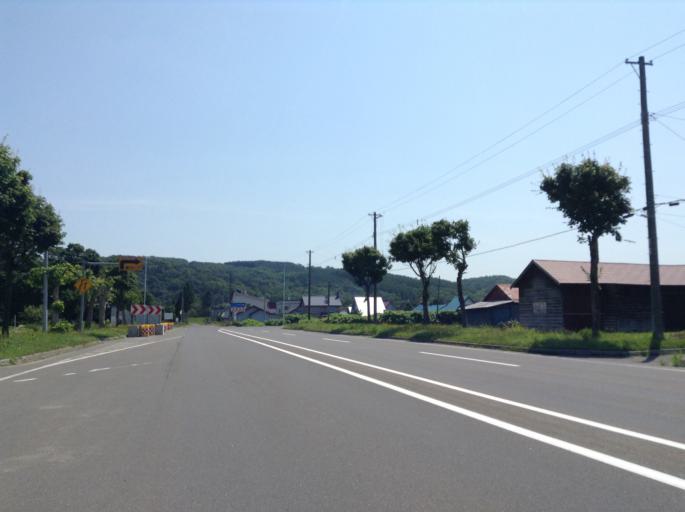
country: JP
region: Hokkaido
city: Nayoro
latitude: 44.3564
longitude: 142.4718
